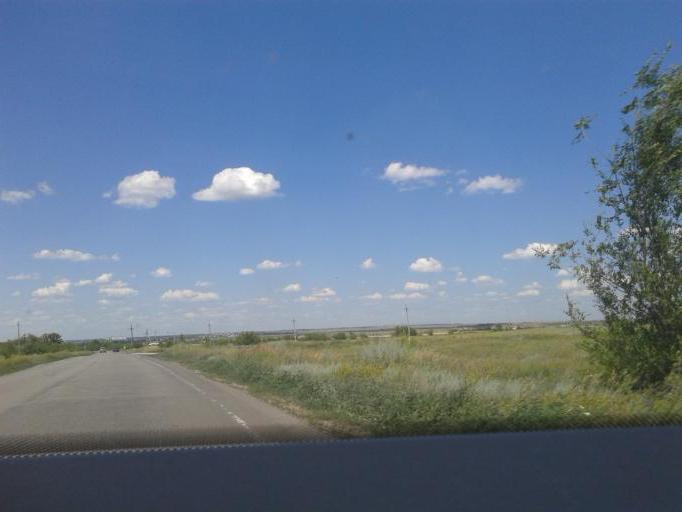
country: RU
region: Volgograd
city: Frolovo
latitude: 49.7140
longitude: 43.6602
